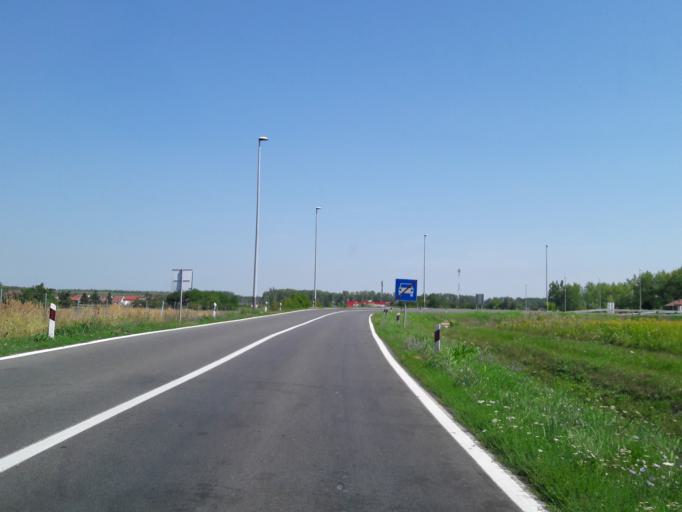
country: HR
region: Osjecko-Baranjska
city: Visnjevac
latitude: 45.5549
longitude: 18.6308
